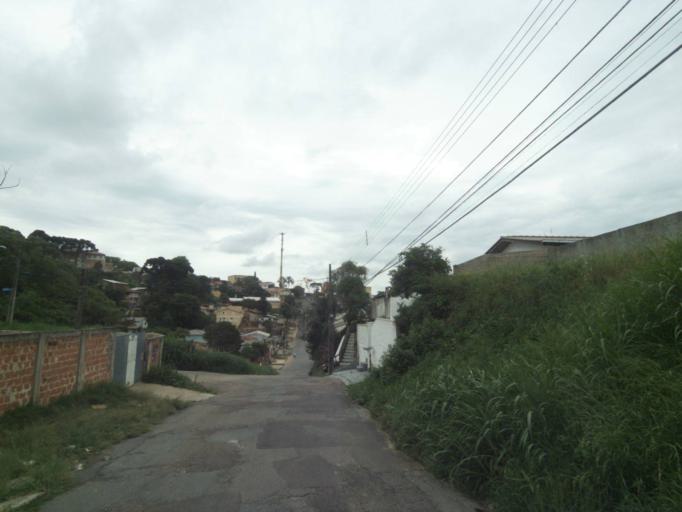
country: BR
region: Parana
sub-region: Curitiba
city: Curitiba
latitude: -25.3917
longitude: -49.2934
